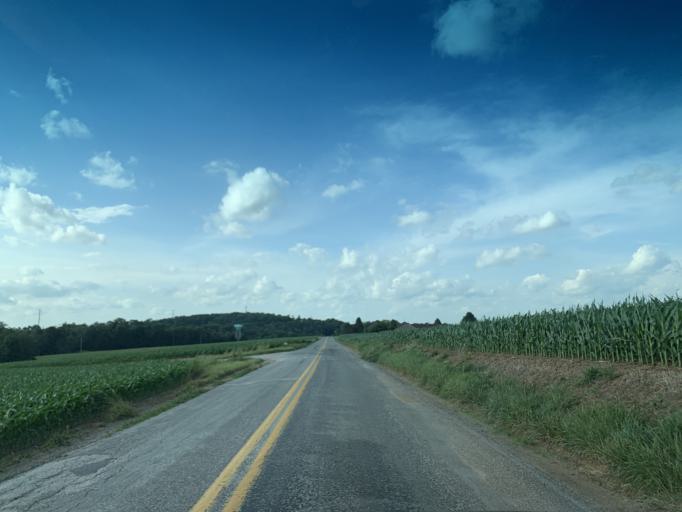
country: US
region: Pennsylvania
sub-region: York County
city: Stewartstown
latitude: 39.7433
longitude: -76.5428
